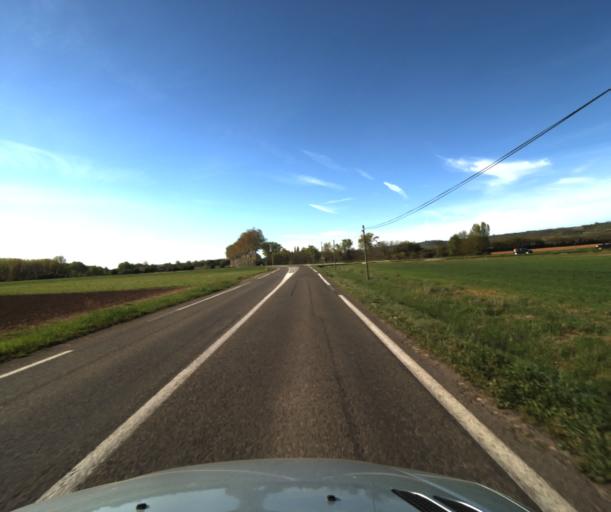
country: FR
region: Midi-Pyrenees
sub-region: Departement du Tarn-et-Garonne
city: Lafrancaise
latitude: 44.0803
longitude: 1.2793
